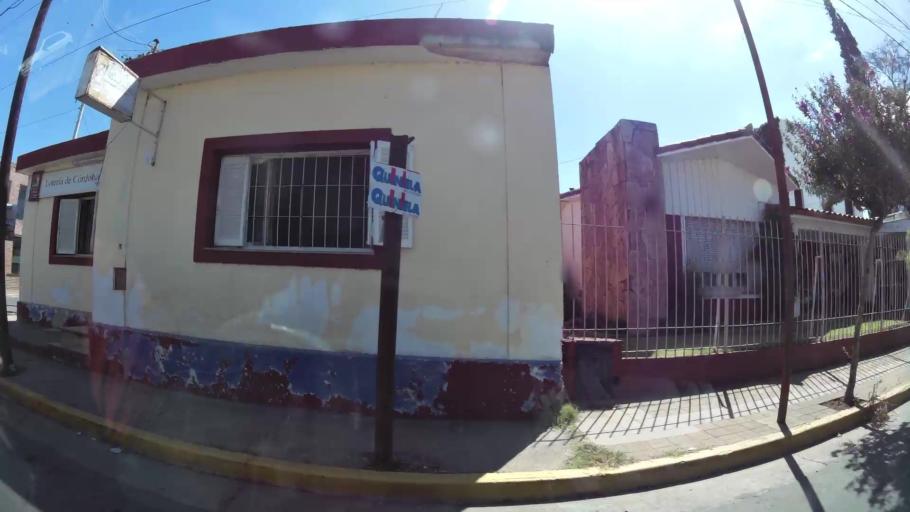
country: AR
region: Cordoba
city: Villa Allende
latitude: -31.2921
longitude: -64.2976
